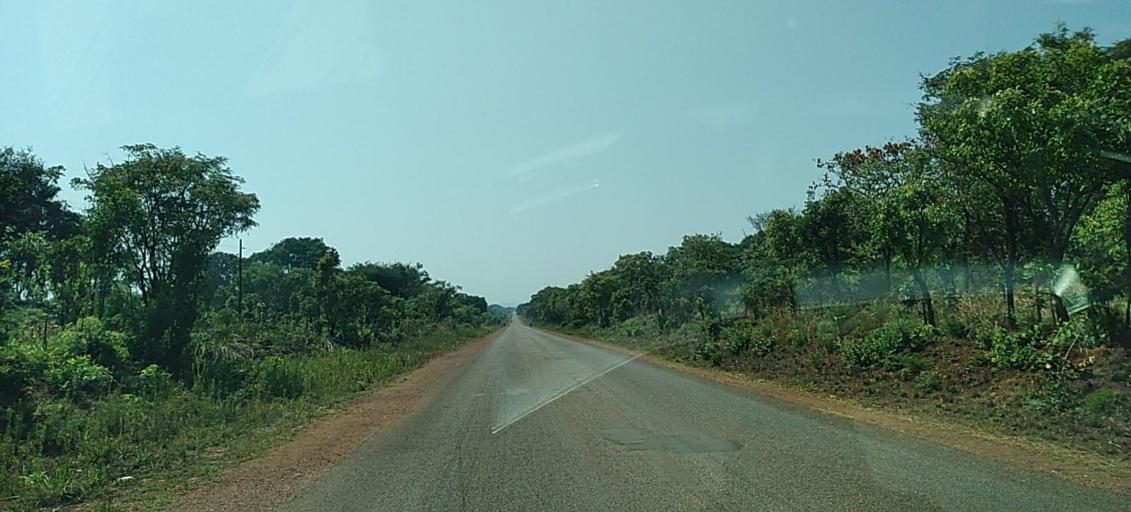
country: ZM
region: North-Western
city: Solwezi
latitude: -12.1203
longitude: 25.5129
